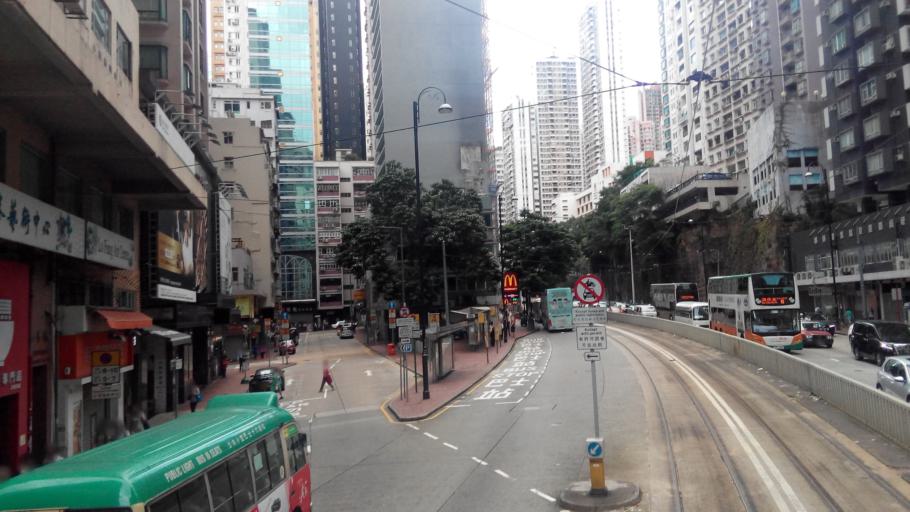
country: HK
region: Wanchai
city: Wan Chai
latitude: 22.2832
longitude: 114.1924
